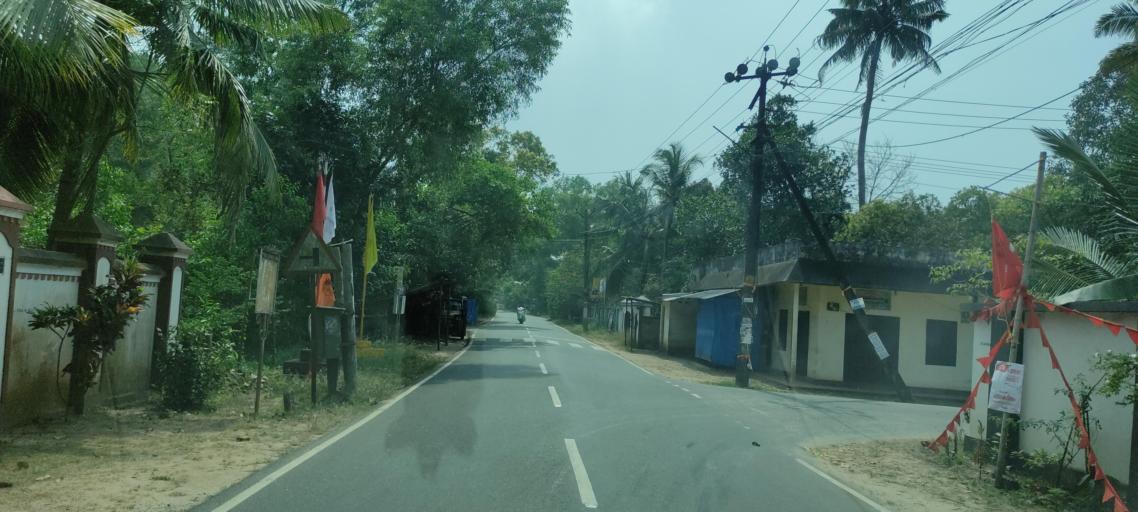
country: IN
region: Kerala
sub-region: Alappuzha
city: Alleppey
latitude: 9.5601
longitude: 76.3341
